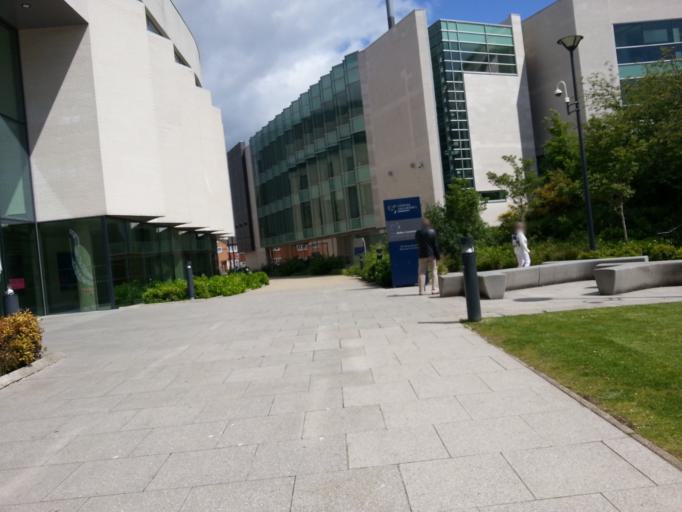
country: GB
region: England
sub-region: Liverpool
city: Liverpool
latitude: 53.4049
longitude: -2.9701
